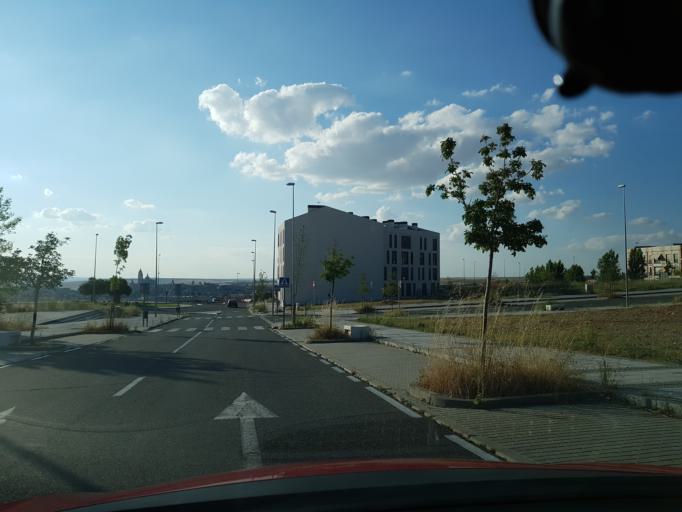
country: ES
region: Castille and Leon
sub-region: Provincia de Segovia
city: Segovia
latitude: 40.9369
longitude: -4.1042
